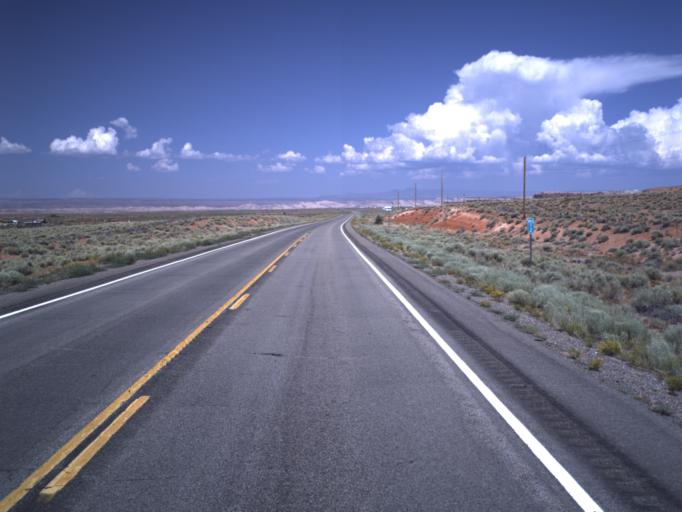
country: US
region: Utah
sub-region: San Juan County
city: Blanding
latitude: 37.1491
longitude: -109.5650
